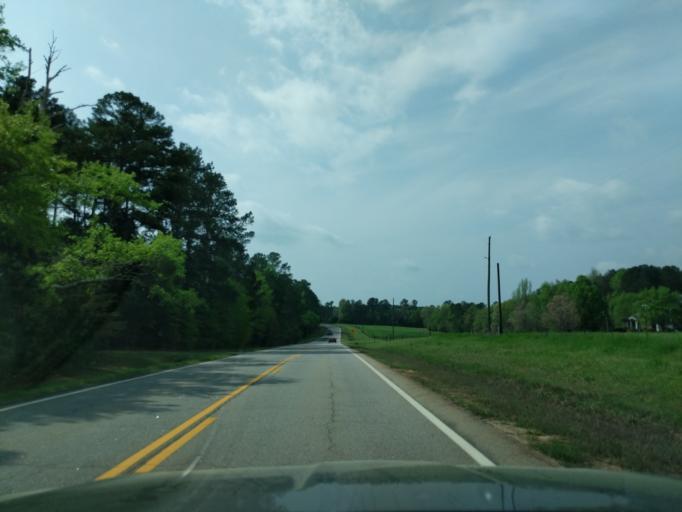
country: US
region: Georgia
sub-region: Lincoln County
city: Lincolnton
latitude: 33.7857
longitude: -82.3809
